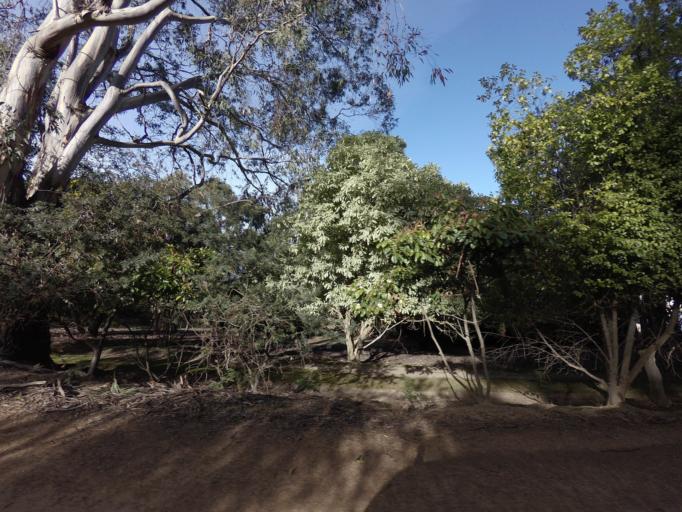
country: AU
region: Tasmania
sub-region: Kingborough
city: Kettering
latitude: -43.1203
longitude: 147.2634
